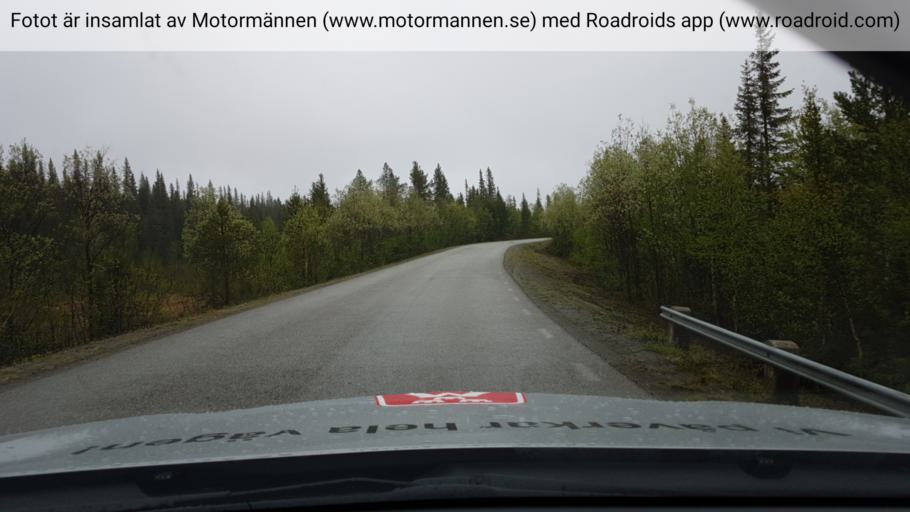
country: SE
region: Jaemtland
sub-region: Krokoms Kommun
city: Valla
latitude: 63.0307
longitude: 13.9500
